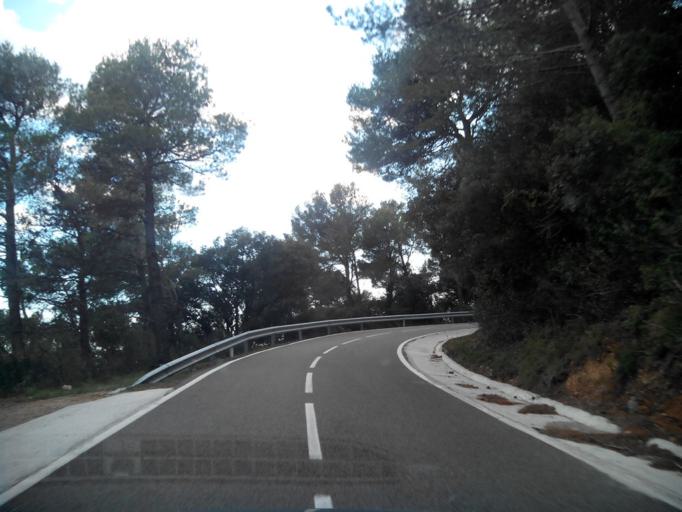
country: ES
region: Catalonia
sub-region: Provincia de Tarragona
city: Vilaplana
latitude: 41.2348
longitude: 1.0607
